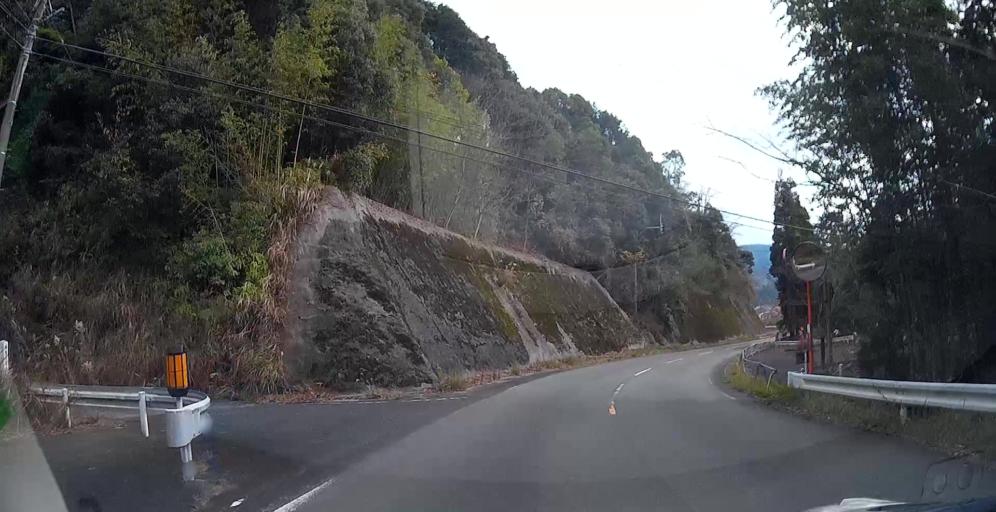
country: JP
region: Kumamoto
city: Yatsushiro
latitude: 32.3681
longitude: 130.5059
